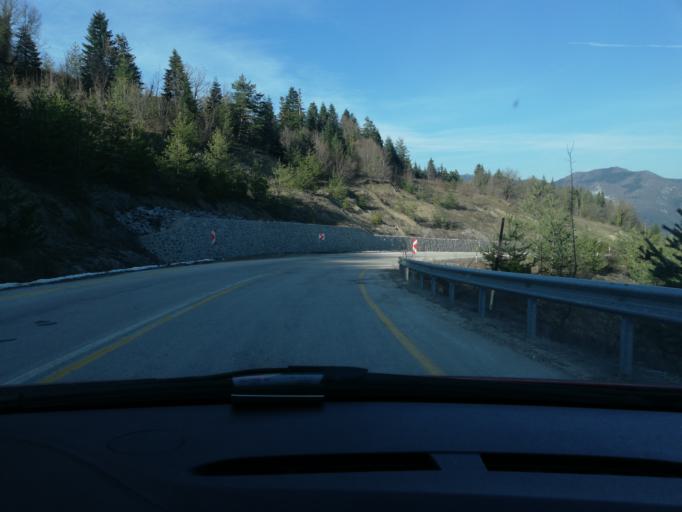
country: TR
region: Kastamonu
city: Senpazar
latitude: 41.7848
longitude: 33.1396
